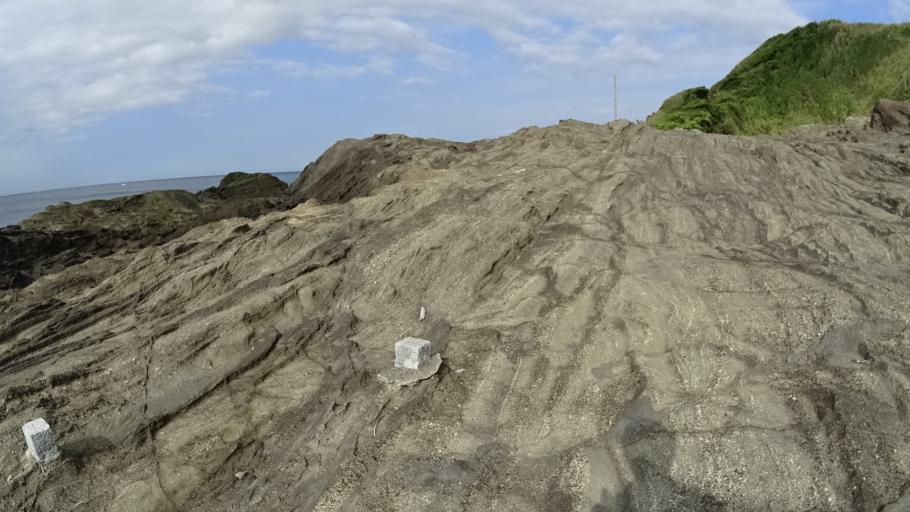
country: JP
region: Kanagawa
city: Miura
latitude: 35.1295
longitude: 139.6274
